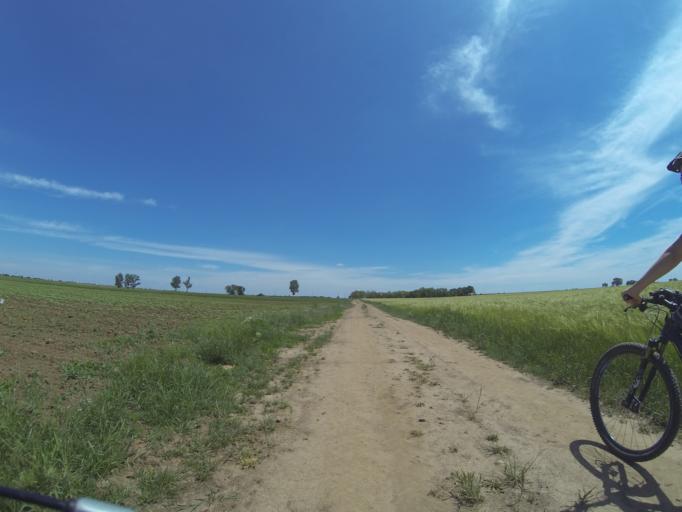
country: RO
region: Dolj
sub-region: Comuna Diosti
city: Radomir
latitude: 44.1463
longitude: 24.1602
